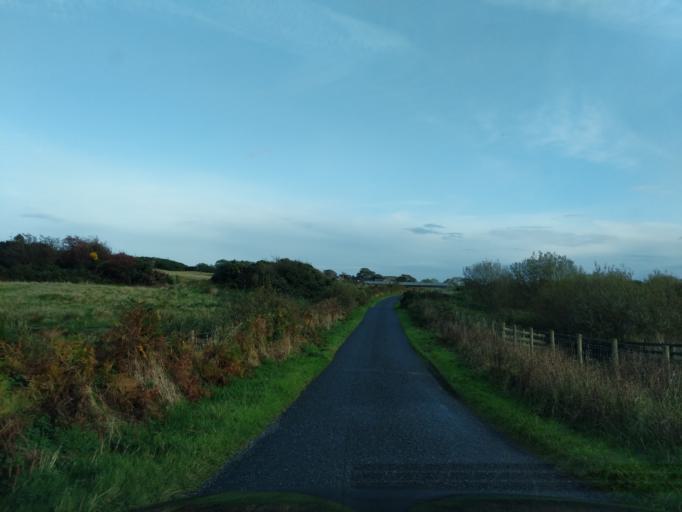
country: GB
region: Scotland
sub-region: Dumfries and Galloway
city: Kirkcudbright
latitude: 54.8380
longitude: -4.1777
